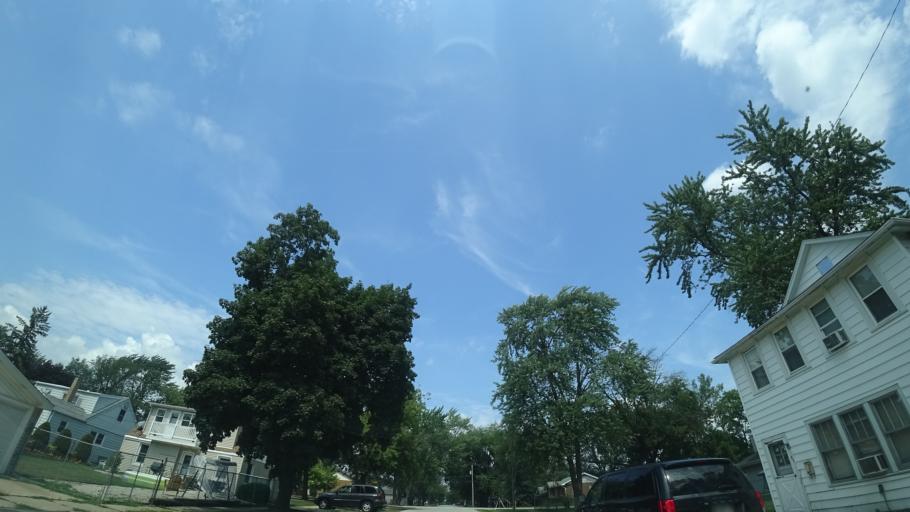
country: US
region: Illinois
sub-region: Cook County
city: Worth
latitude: 41.6847
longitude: -87.7951
